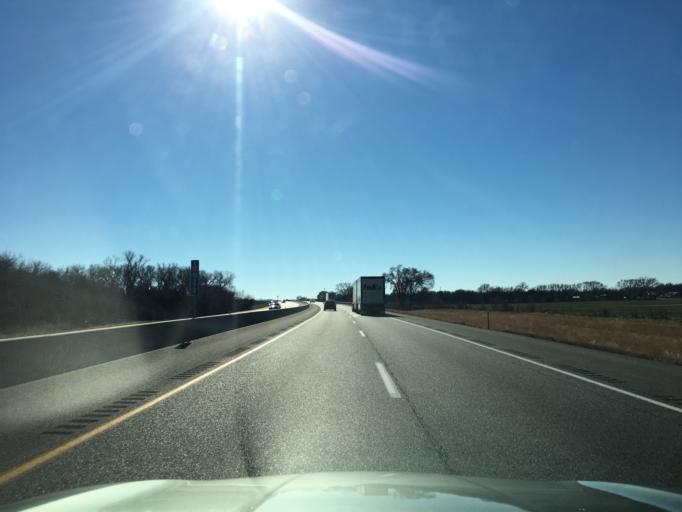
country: US
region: Kansas
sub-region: Sumner County
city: Belle Plaine
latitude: 37.3970
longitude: -97.3261
